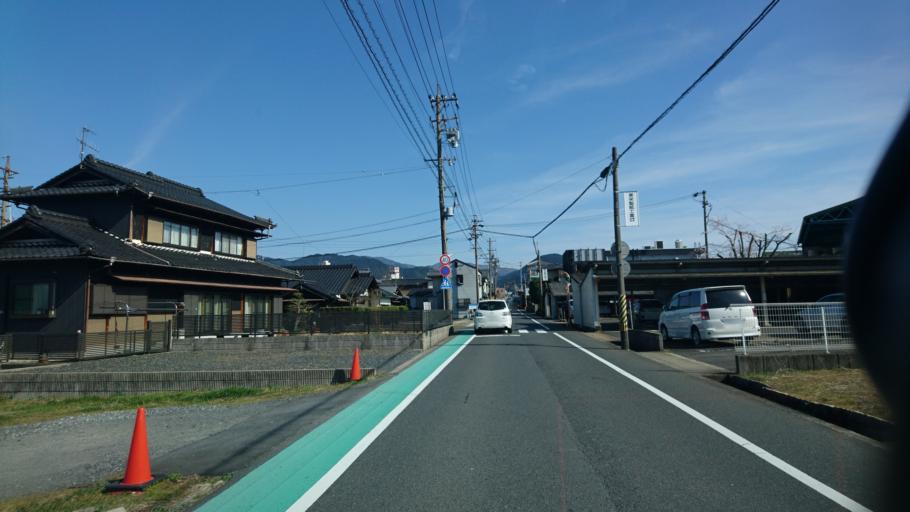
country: JP
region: Gifu
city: Nakatsugawa
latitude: 35.4574
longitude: 137.4073
